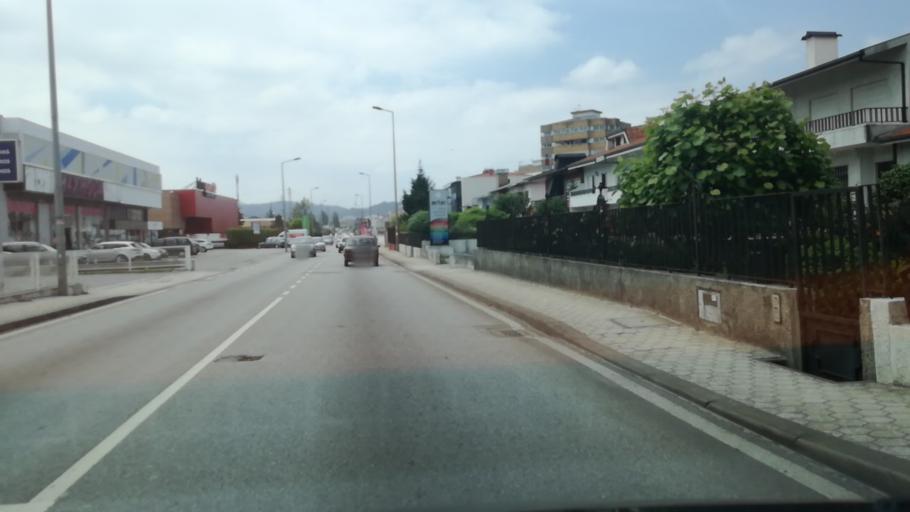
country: PT
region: Porto
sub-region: Trofa
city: Bougado
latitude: 41.3315
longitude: -8.5640
